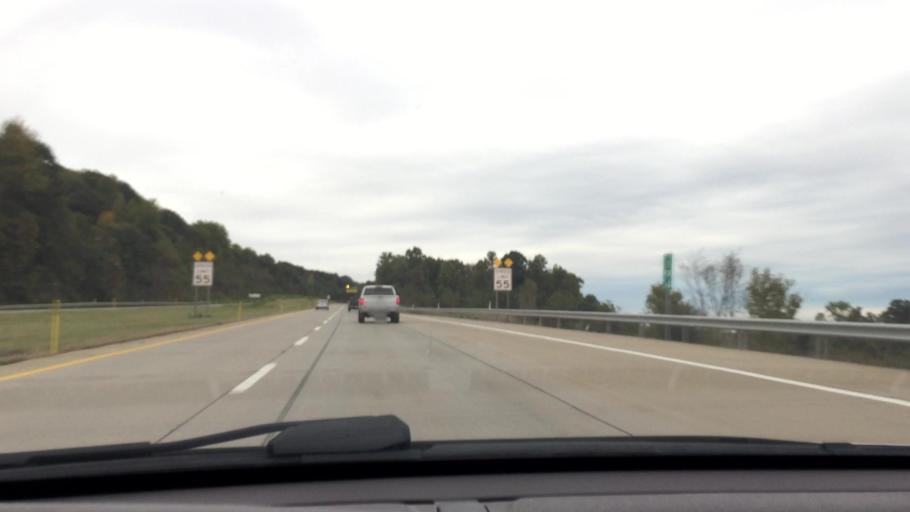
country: US
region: Pennsylvania
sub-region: Lawrence County
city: New Beaver
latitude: 40.9262
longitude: -80.3877
